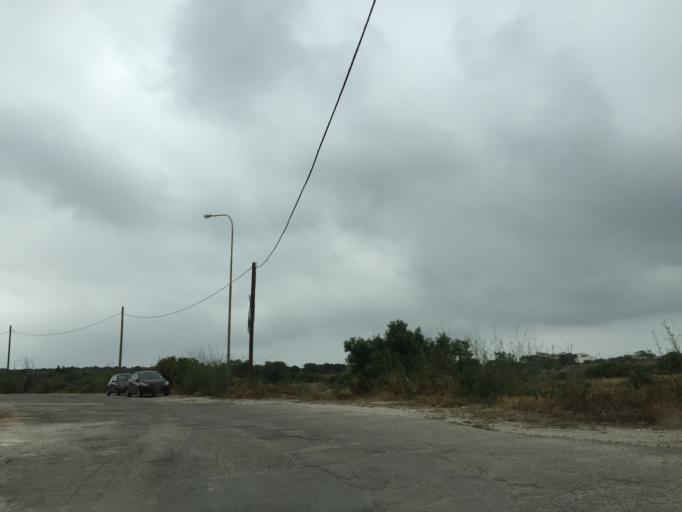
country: MT
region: L-Imgarr
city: Imgarr
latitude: 35.9228
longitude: 14.3684
